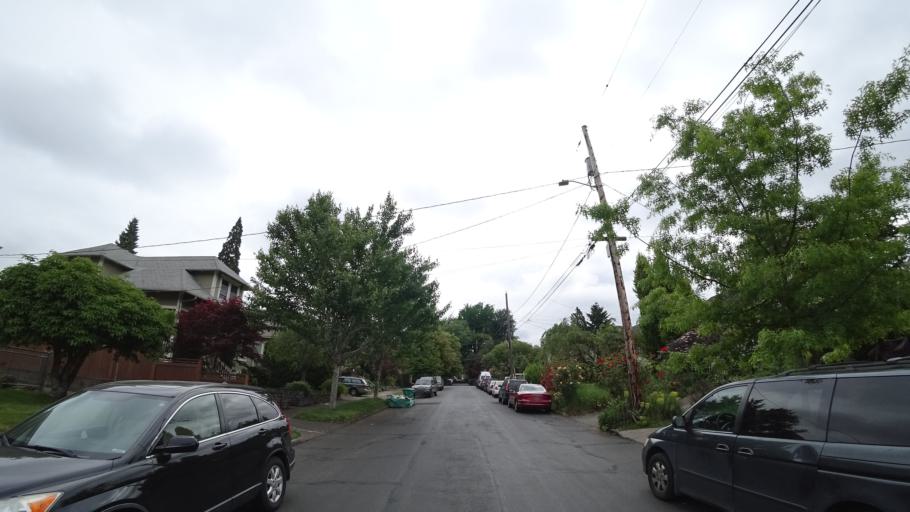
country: US
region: Oregon
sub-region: Multnomah County
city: Portland
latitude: 45.4998
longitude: -122.6386
